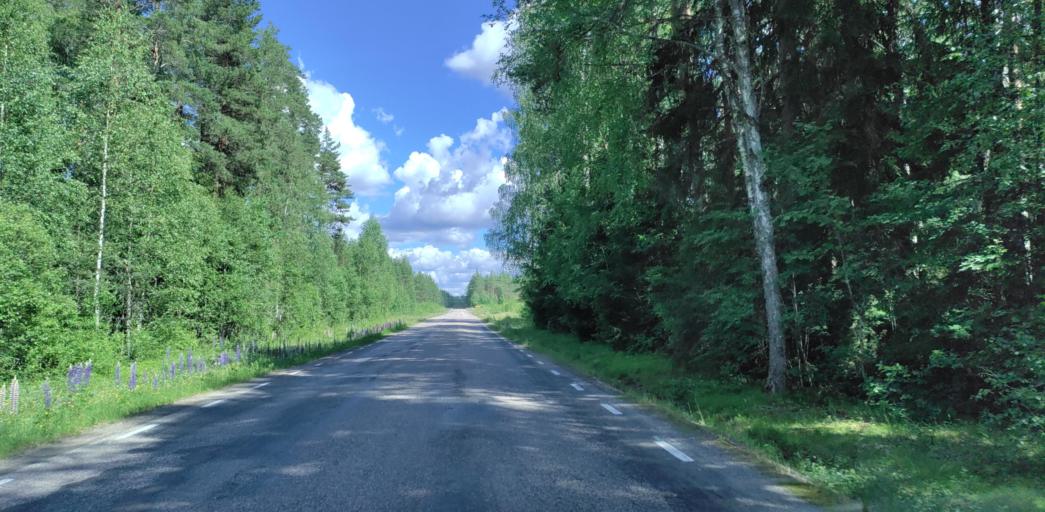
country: SE
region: Vaermland
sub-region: Munkfors Kommun
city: Munkfors
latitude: 59.9697
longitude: 13.5208
